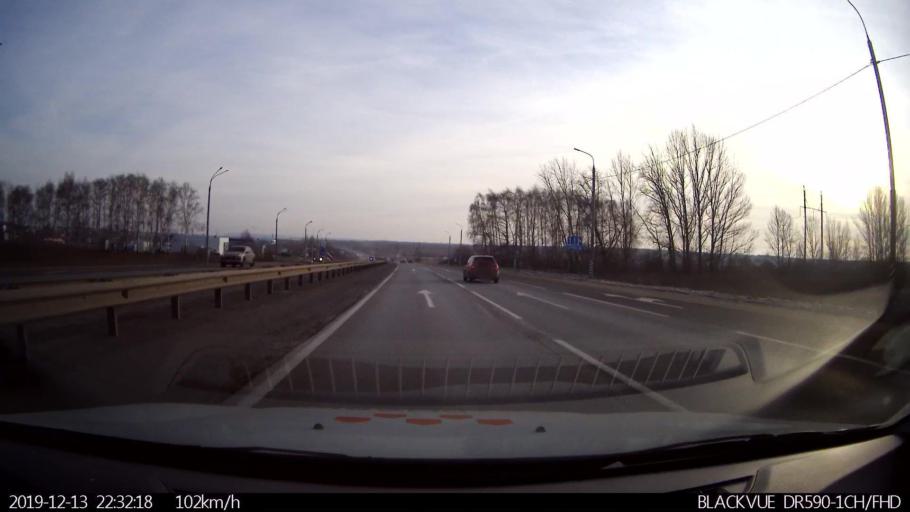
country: RU
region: Nizjnij Novgorod
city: Afonino
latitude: 56.2068
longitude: 44.0883
